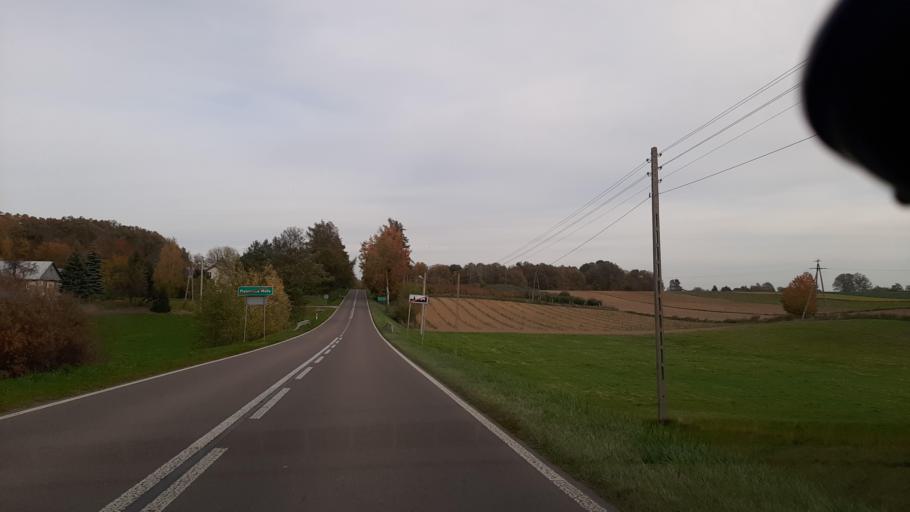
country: PL
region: Lublin Voivodeship
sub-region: Powiat pulawski
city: Naleczow
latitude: 51.3261
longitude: 22.2408
